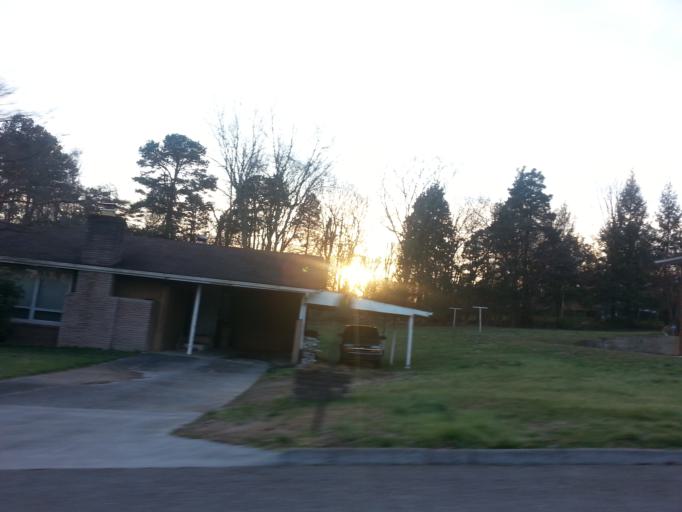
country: US
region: Tennessee
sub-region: Knox County
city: Knoxville
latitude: 36.0195
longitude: -83.8783
